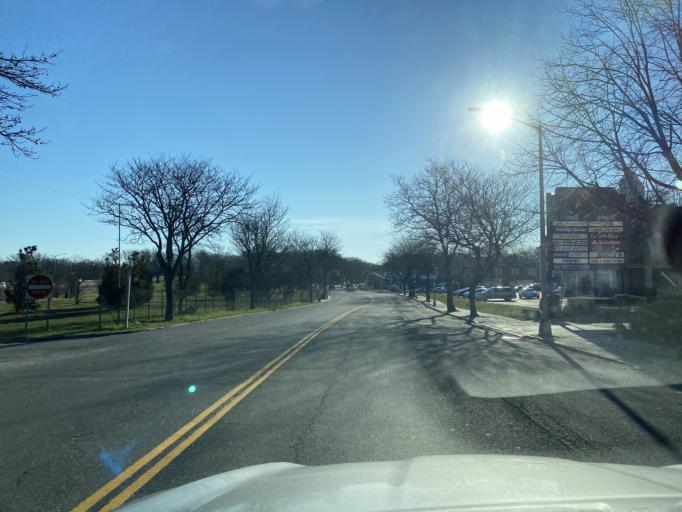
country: US
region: New York
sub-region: Nassau County
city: East Atlantic Beach
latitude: 40.7889
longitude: -73.7862
